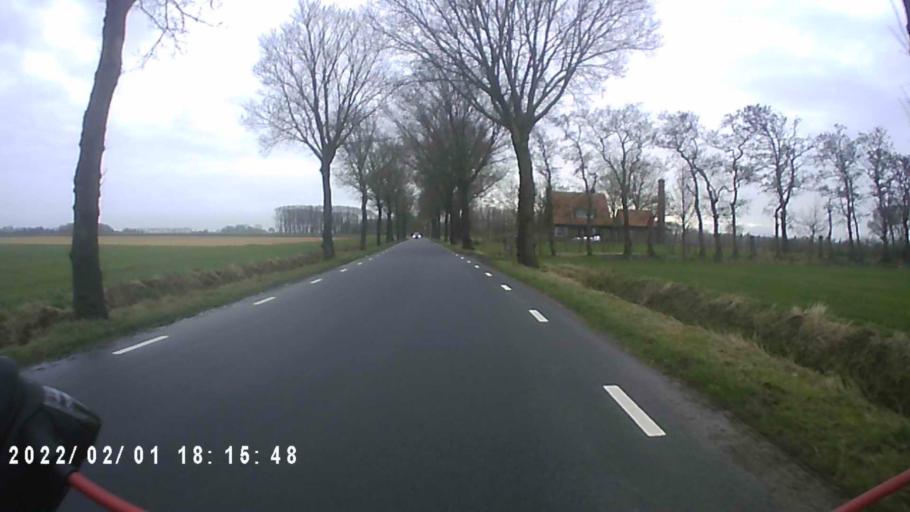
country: NL
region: Groningen
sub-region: Gemeente De Marne
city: Ulrum
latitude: 53.3474
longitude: 6.3325
